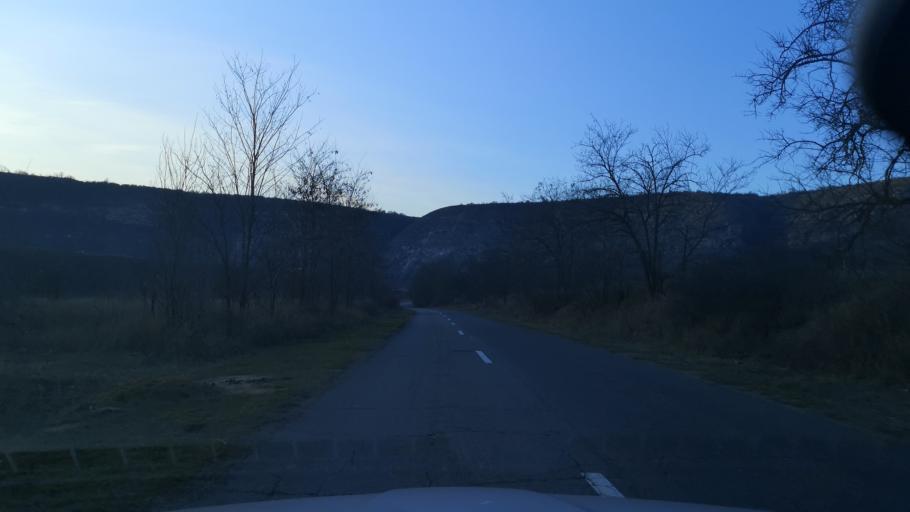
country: MD
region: Telenesti
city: Cocieri
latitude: 47.3061
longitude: 28.9694
